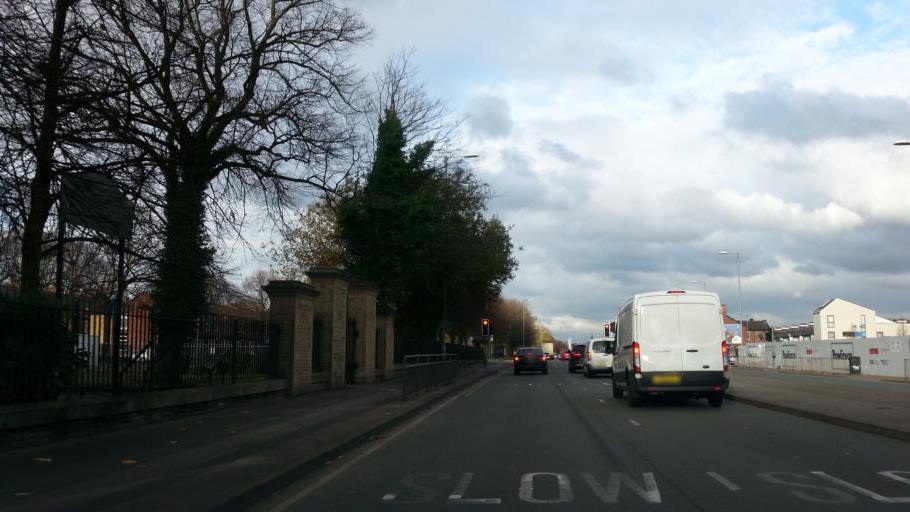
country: GB
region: England
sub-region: Manchester
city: Hulme
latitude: 53.4509
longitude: -2.2450
